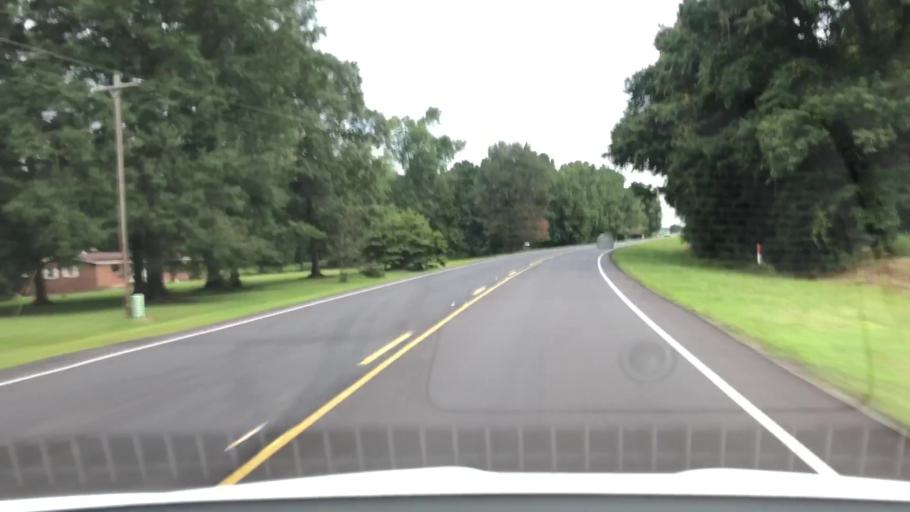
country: US
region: North Carolina
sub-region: Jones County
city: Maysville
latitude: 34.8870
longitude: -77.2128
